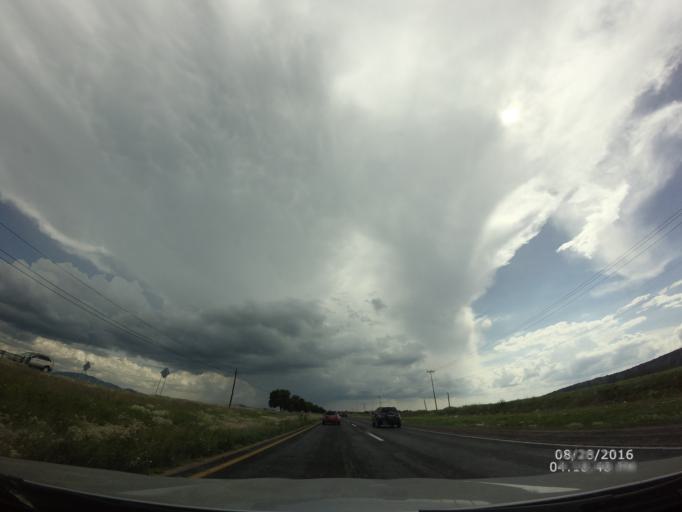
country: MX
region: Hidalgo
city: Zapotlan de Juarez
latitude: 19.9613
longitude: -98.8622
